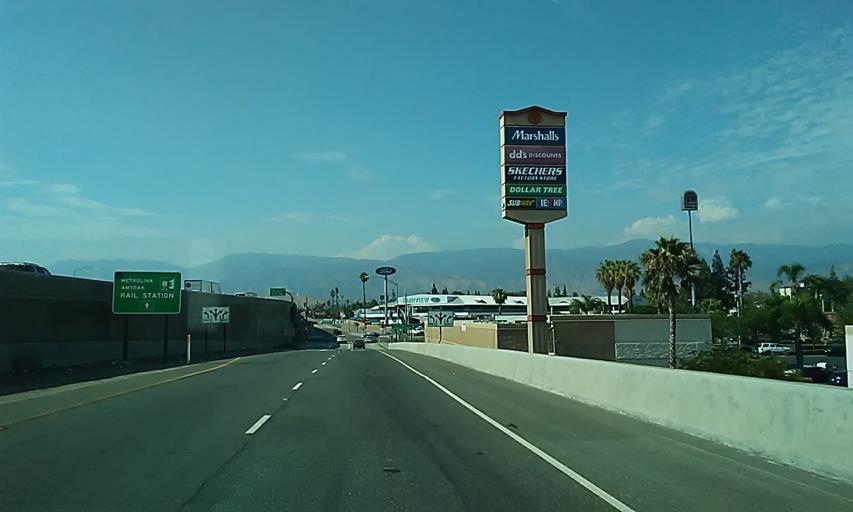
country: US
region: California
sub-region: San Bernardino County
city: San Bernardino
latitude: 34.1011
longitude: -117.3015
